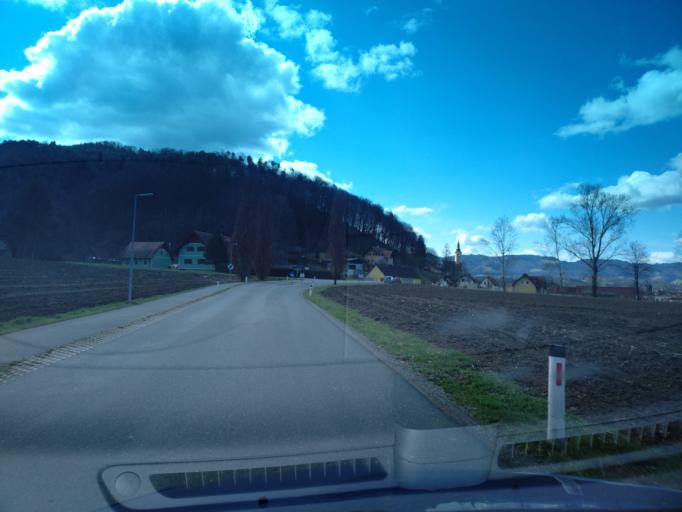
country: AT
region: Styria
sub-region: Politischer Bezirk Leibnitz
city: Sankt Johann im Saggautal
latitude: 46.7078
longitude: 15.4040
